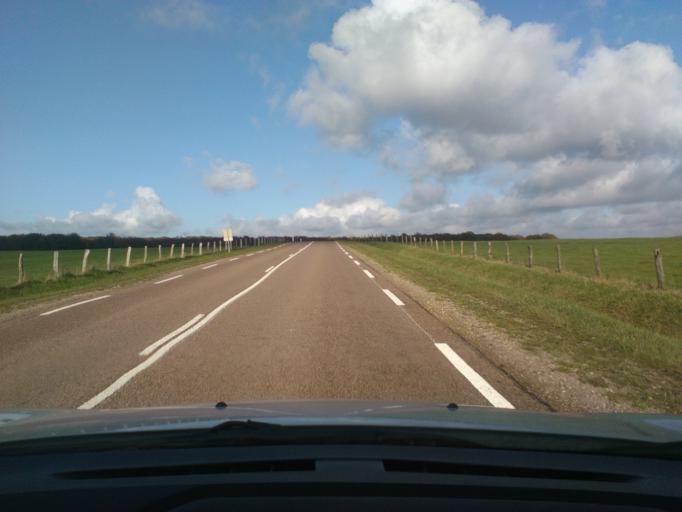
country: FR
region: Lorraine
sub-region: Departement des Vosges
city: Mirecourt
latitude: 48.3448
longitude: 6.1152
